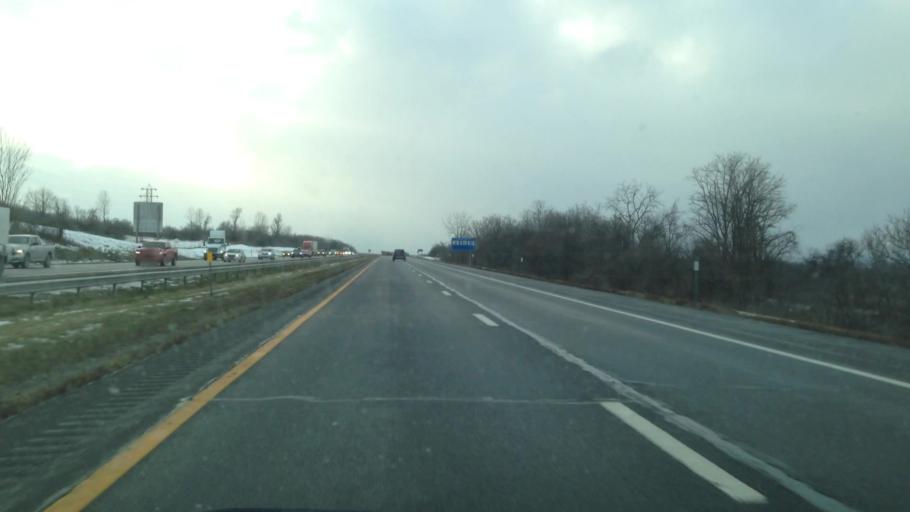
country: US
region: New York
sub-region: Montgomery County
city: Amsterdam
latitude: 42.9198
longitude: -74.1817
